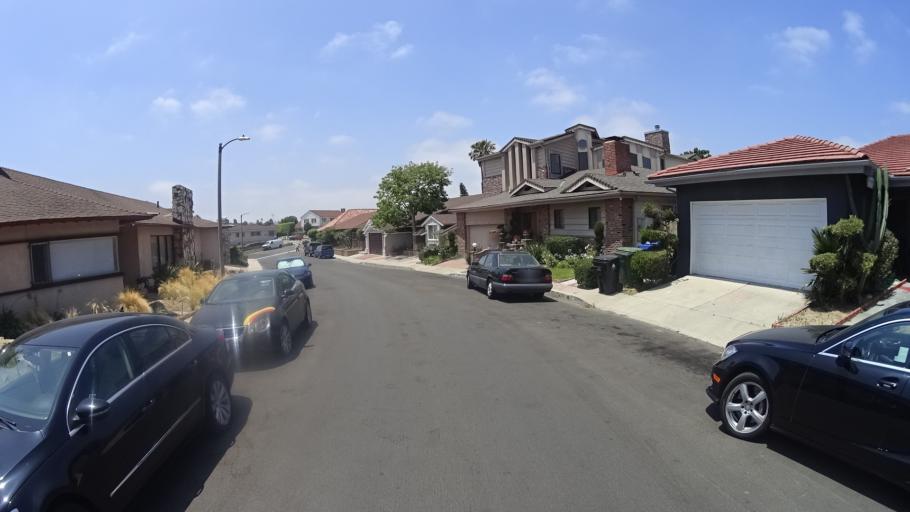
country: US
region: California
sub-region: Los Angeles County
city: View Park-Windsor Hills
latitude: 34.0076
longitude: -118.3495
